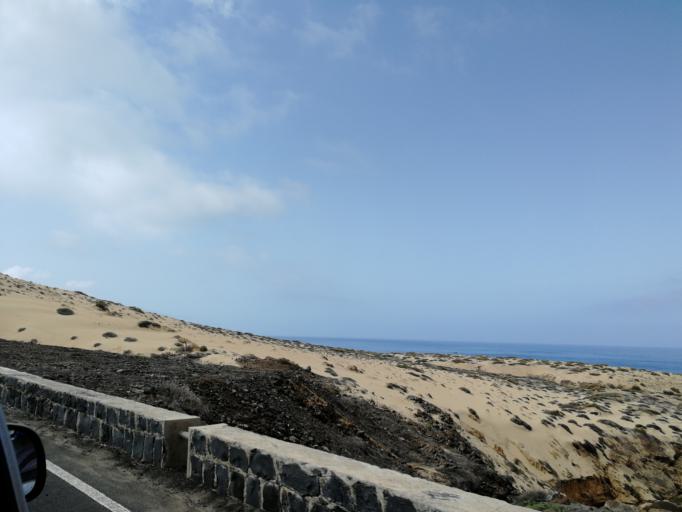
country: CV
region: Sao Vicente
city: Mindelo
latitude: 16.8610
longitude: -24.8913
